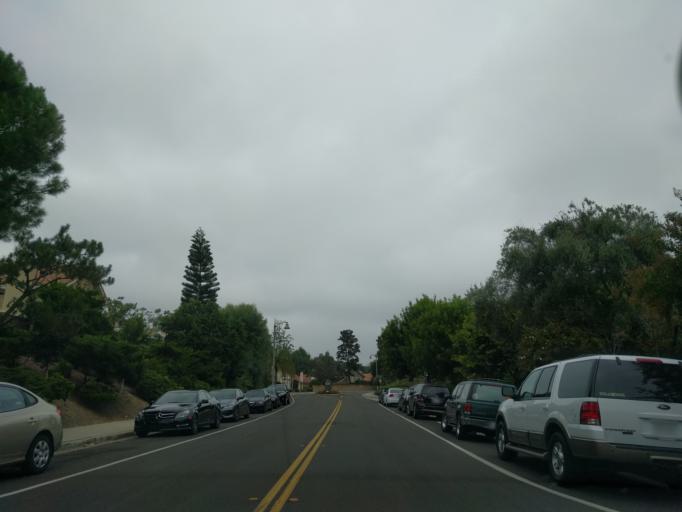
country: US
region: California
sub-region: Orange County
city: Mission Viejo
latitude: 33.5880
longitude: -117.6634
